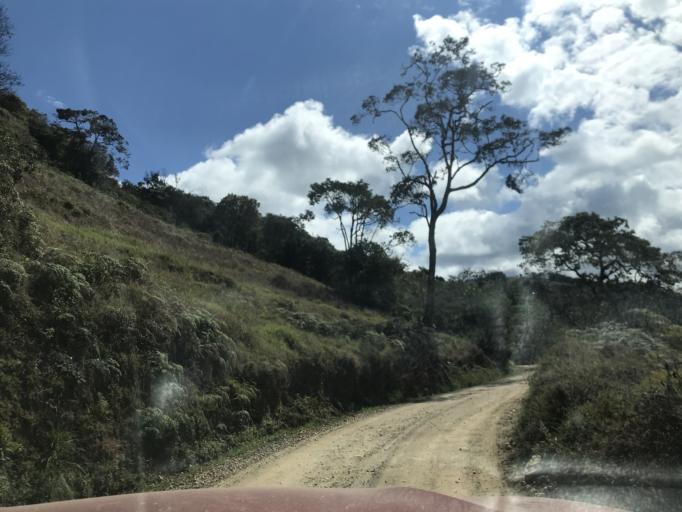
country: PE
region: Cajamarca
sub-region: Provincia de Chota
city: Querocoto
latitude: -6.3506
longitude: -79.0396
